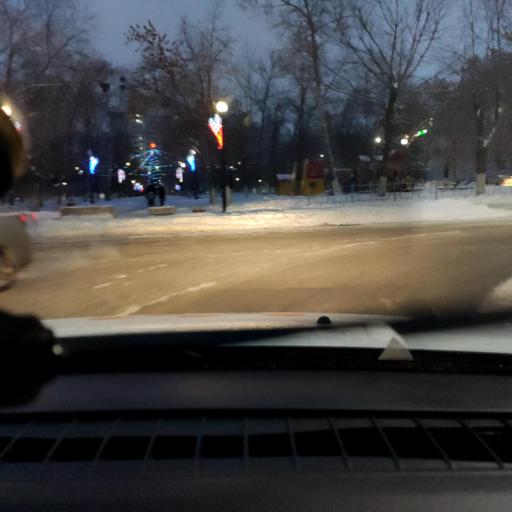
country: RU
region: Samara
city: Novokuybyshevsk
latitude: 53.0961
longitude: 49.9568
